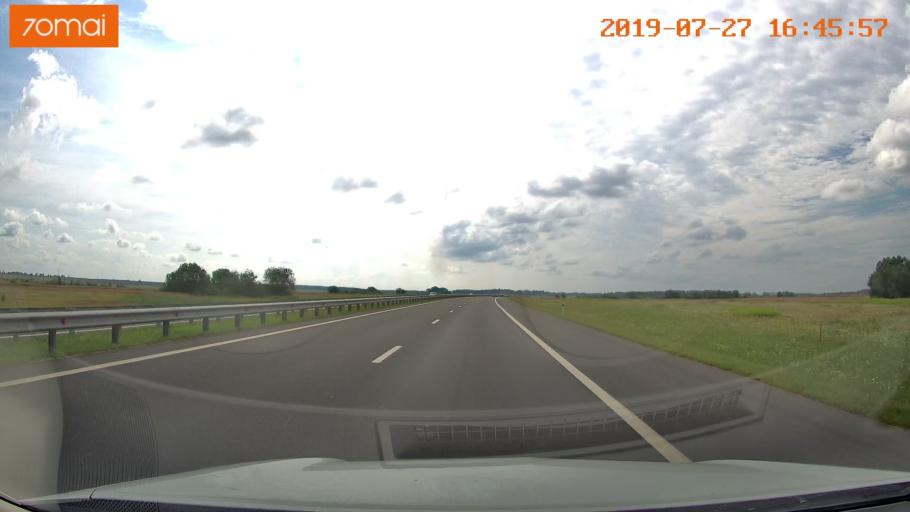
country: RU
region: Kaliningrad
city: Gvardeysk
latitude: 54.6675
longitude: 21.0351
